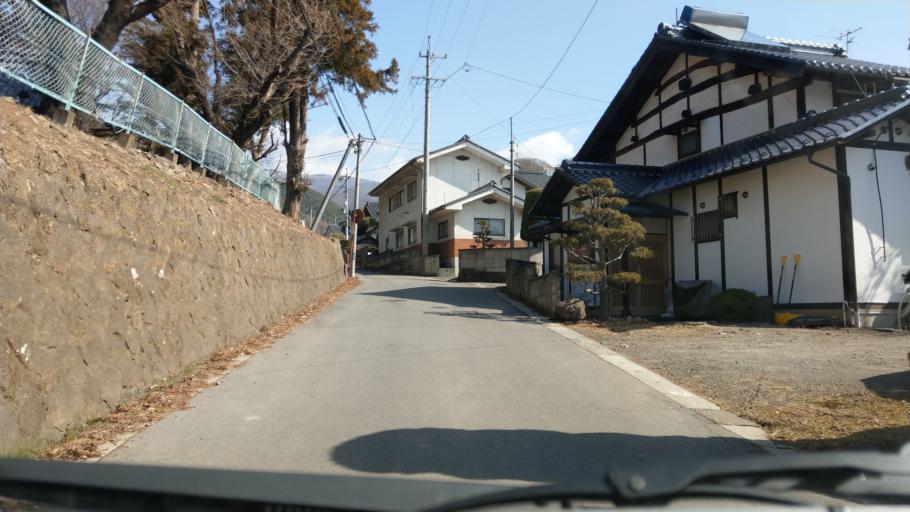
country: JP
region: Nagano
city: Ueda
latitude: 36.3765
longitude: 138.3525
